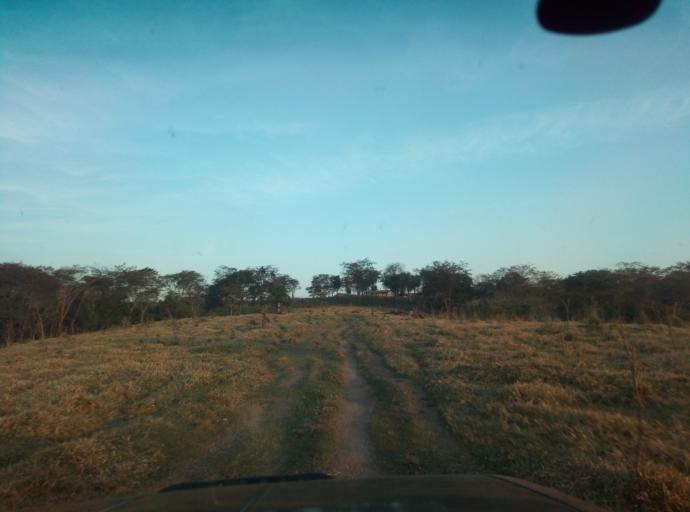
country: PY
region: Caaguazu
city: Yhu
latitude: -25.2044
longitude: -56.1068
